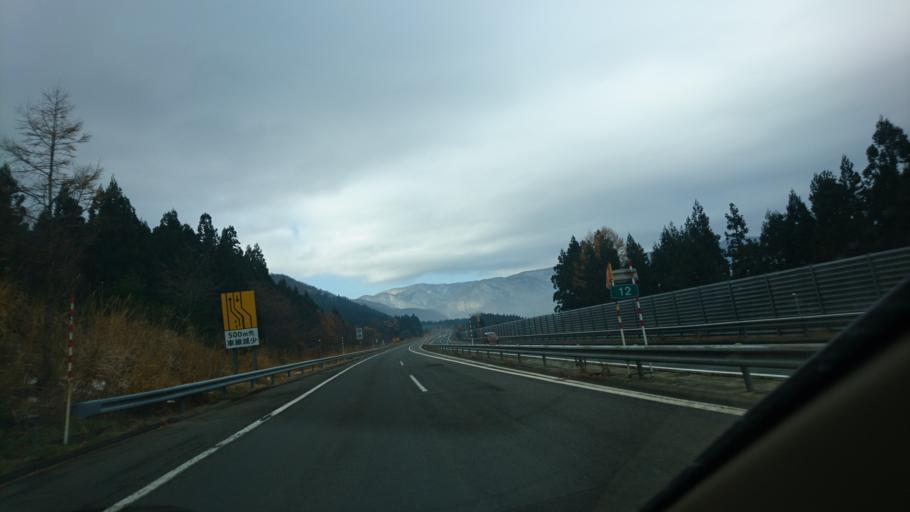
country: JP
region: Iwate
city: Kitakami
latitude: 39.2948
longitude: 140.9475
